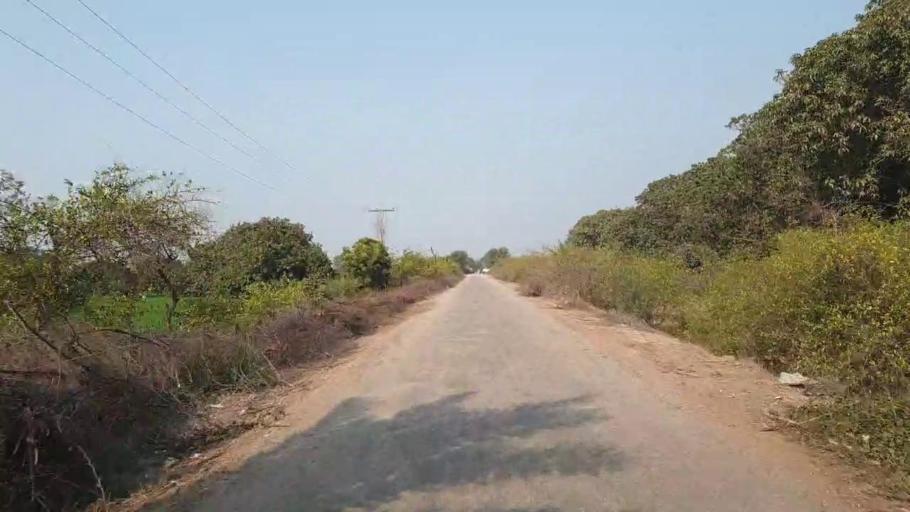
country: PK
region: Sindh
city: Hala
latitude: 25.8444
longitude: 68.4615
